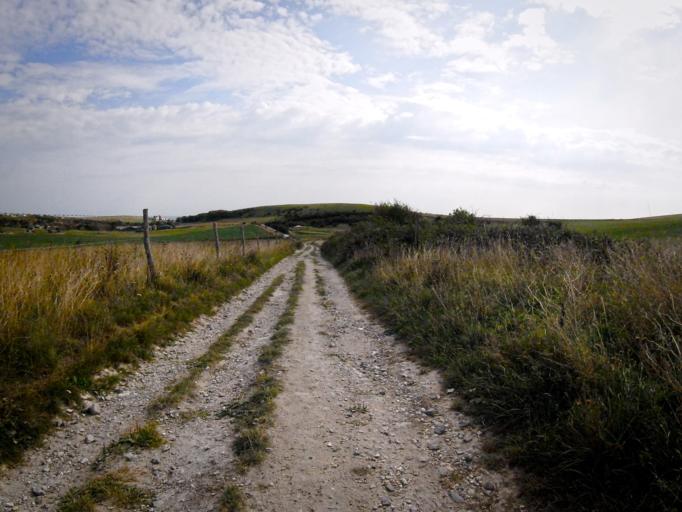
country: GB
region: England
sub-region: Brighton and Hove
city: Rottingdean
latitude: 50.8227
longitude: -0.0847
